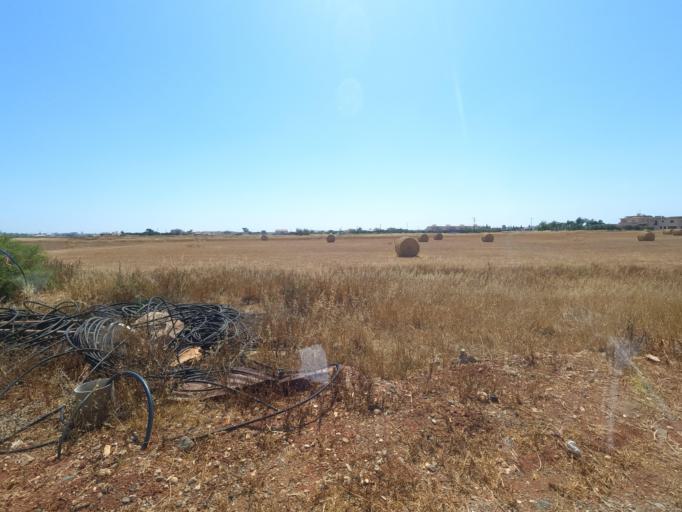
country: CY
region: Ammochostos
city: Liopetri
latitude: 35.0183
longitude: 33.8885
